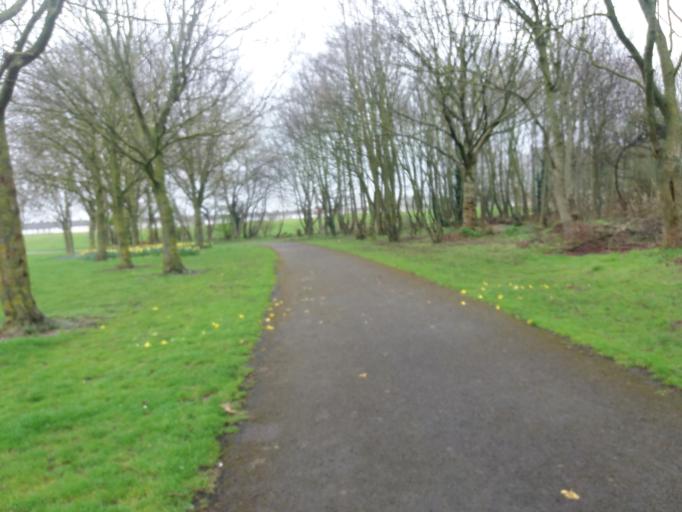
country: IE
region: Leinster
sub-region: Dublin City
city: Finglas
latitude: 53.3982
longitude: -6.2836
